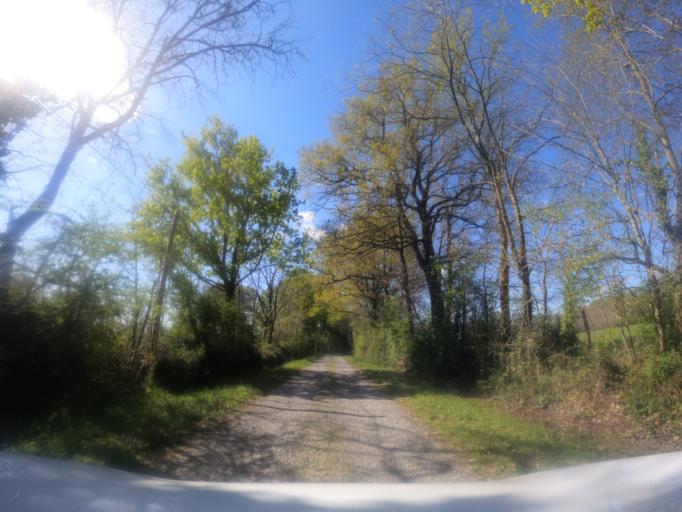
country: FR
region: Pays de la Loire
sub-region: Departement de la Vendee
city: Saint-Vincent-sur-Graon
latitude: 46.5195
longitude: -1.3679
